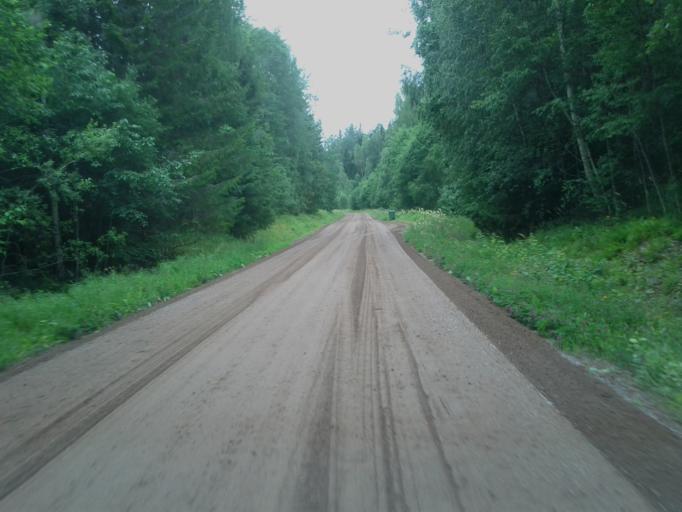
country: SE
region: Dalarna
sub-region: Borlange Kommun
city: Borlaenge
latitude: 60.3419
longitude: 15.4239
